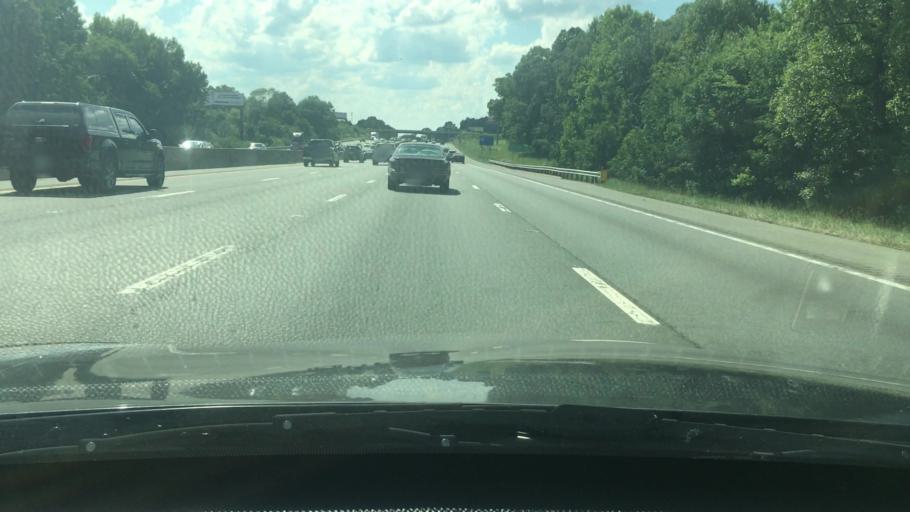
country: US
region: North Carolina
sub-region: Alamance County
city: Haw River
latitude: 36.0666
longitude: -79.3245
